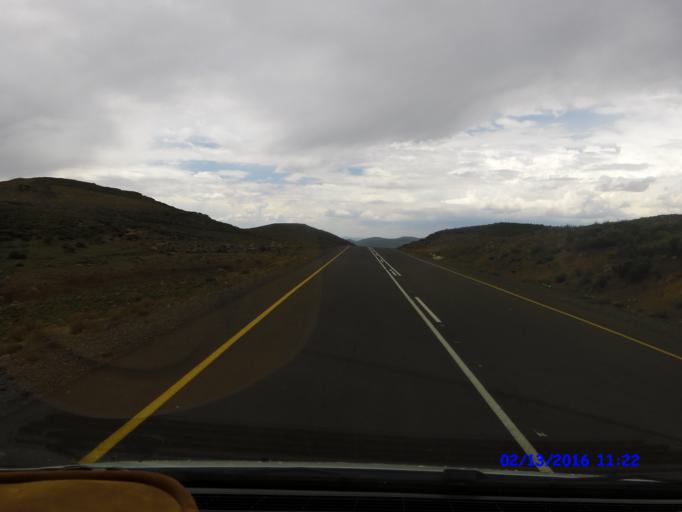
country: LS
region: Maseru
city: Nako
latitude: -29.7593
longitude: 27.9818
